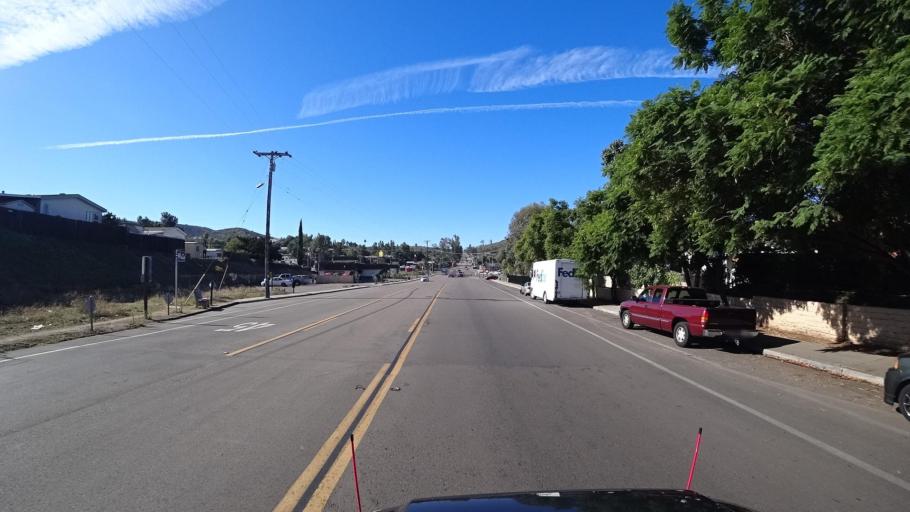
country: US
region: California
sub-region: San Diego County
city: Winter Gardens
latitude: 32.8339
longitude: -116.9042
